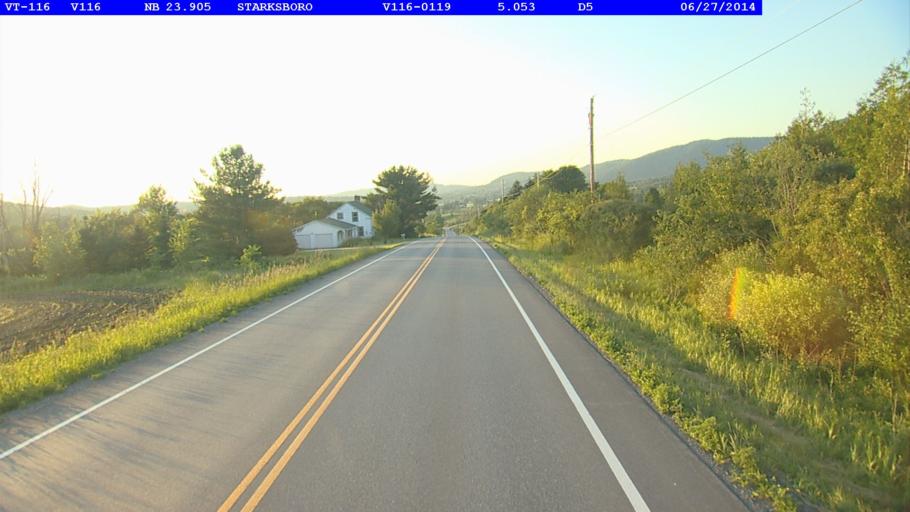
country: US
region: Vermont
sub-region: Chittenden County
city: Hinesburg
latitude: 44.2571
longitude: -73.0637
